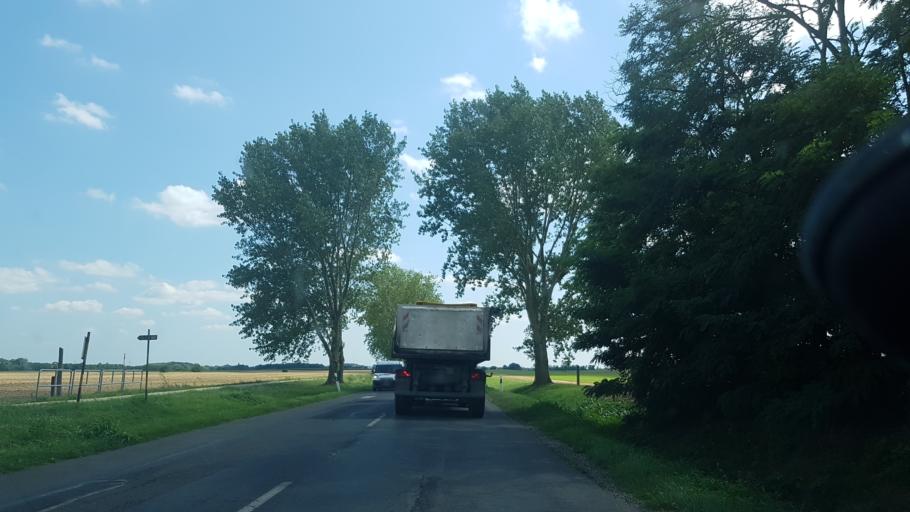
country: HU
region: Somogy
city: Kethely
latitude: 46.6177
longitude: 17.3987
